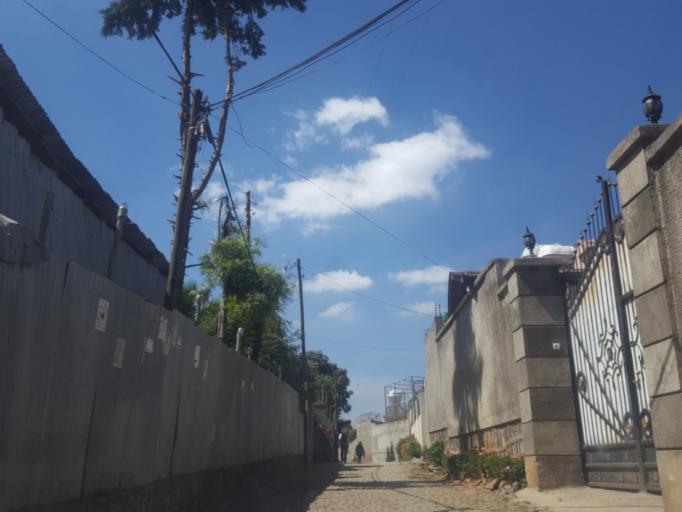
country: ET
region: Adis Abeba
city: Addis Ababa
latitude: 9.0512
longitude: 38.7309
